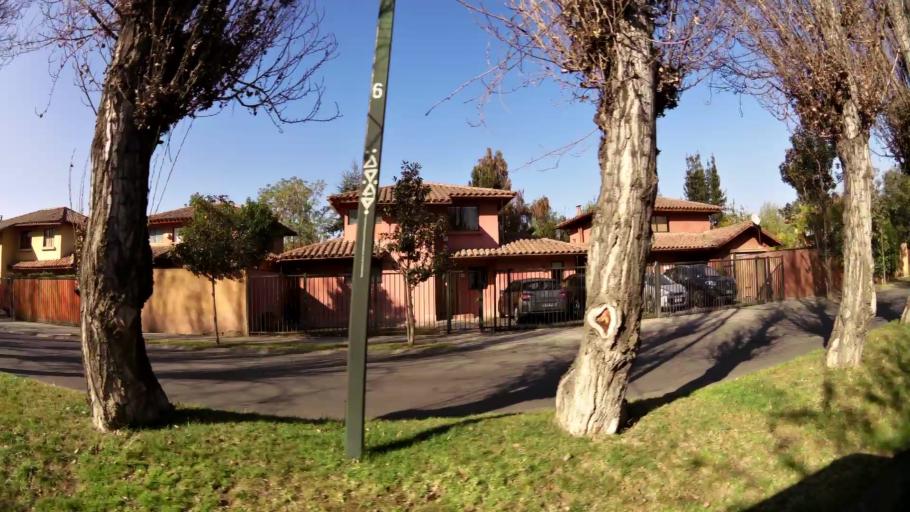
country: CL
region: Santiago Metropolitan
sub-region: Provincia de Chacabuco
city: Chicureo Abajo
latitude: -33.3580
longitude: -70.6682
